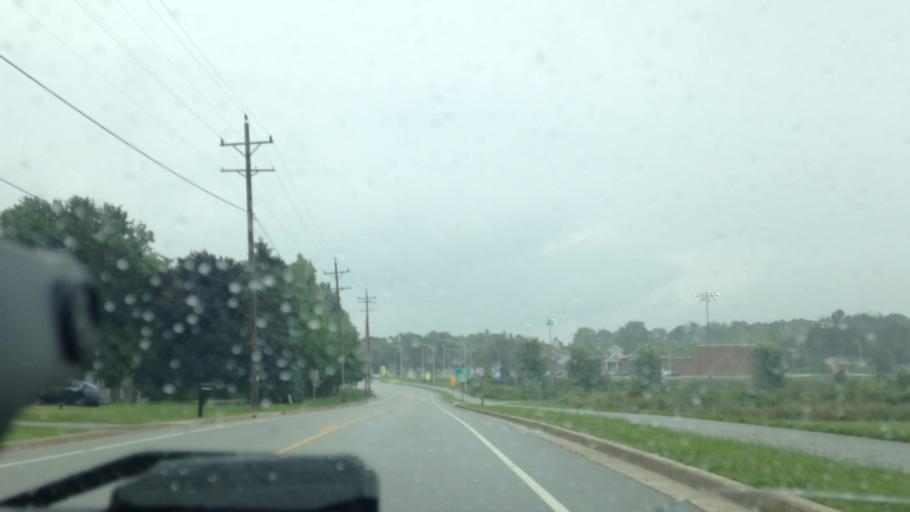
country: US
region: Wisconsin
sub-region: Washington County
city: Richfield
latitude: 43.2534
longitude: -88.1929
